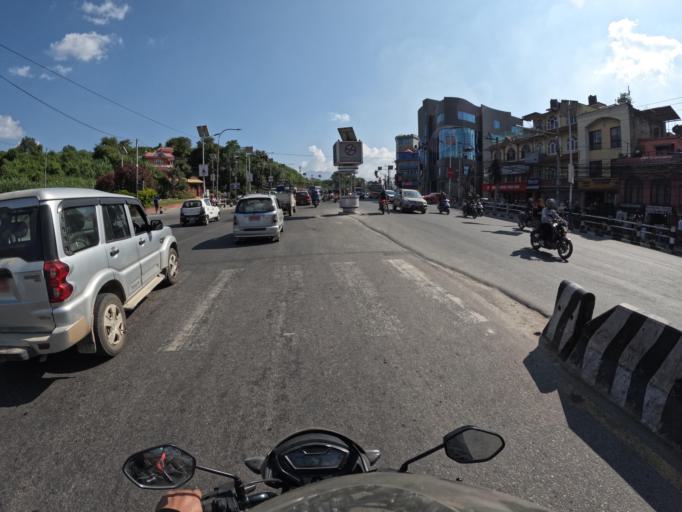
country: NP
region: Central Region
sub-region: Bagmati Zone
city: Kathmandu
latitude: 27.6840
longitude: 85.3490
